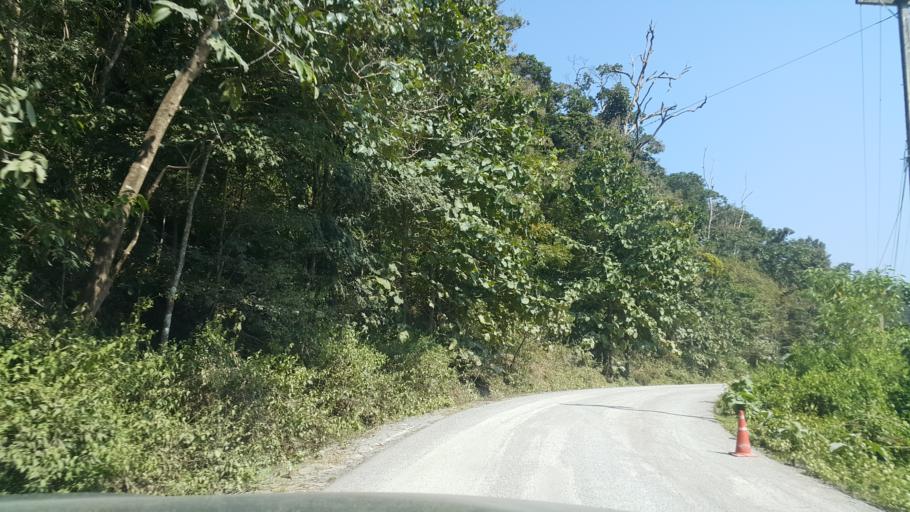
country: TH
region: Chiang Mai
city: Samoeng
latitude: 18.8850
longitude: 98.6049
